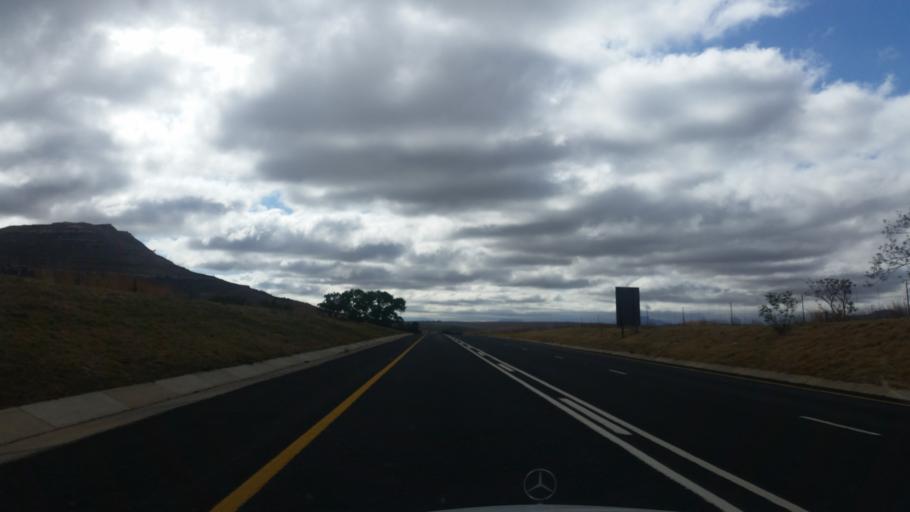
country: ZA
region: Orange Free State
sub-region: Thabo Mofutsanyana District Municipality
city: Phuthaditjhaba
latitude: -28.3128
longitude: 28.7415
